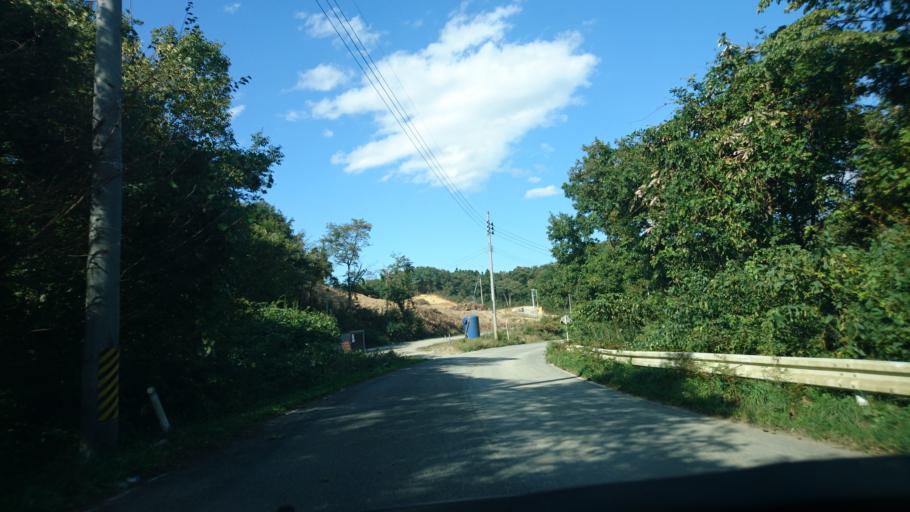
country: JP
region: Iwate
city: Ichinoseki
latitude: 38.8750
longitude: 141.0459
